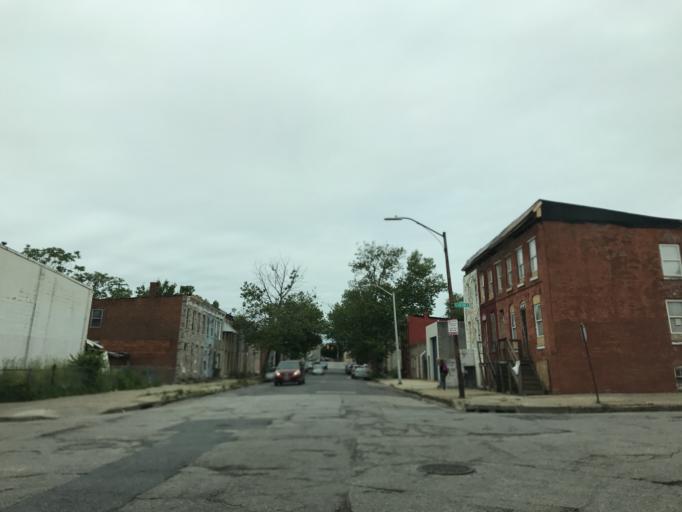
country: US
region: Maryland
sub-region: City of Baltimore
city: Baltimore
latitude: 39.2811
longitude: -76.6445
